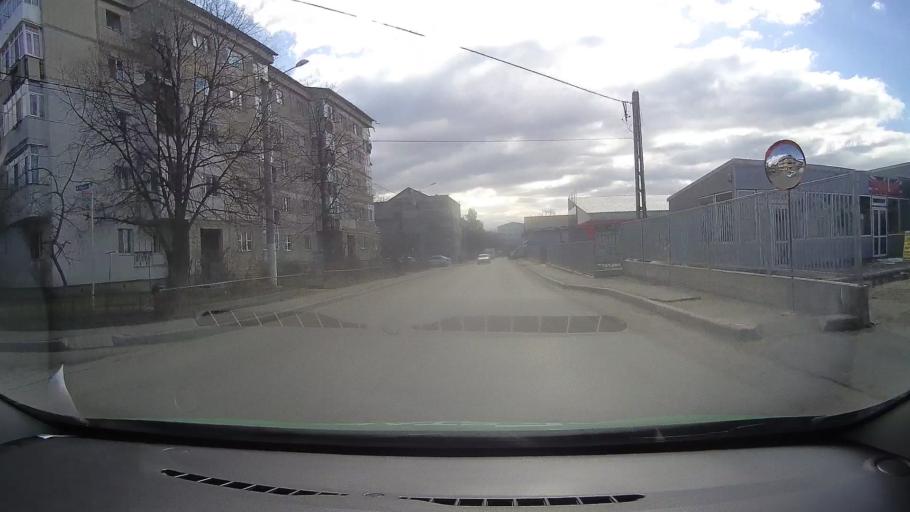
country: RO
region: Dambovita
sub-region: Oras Pucioasa
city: Pucioasa
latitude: 45.0733
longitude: 25.4325
